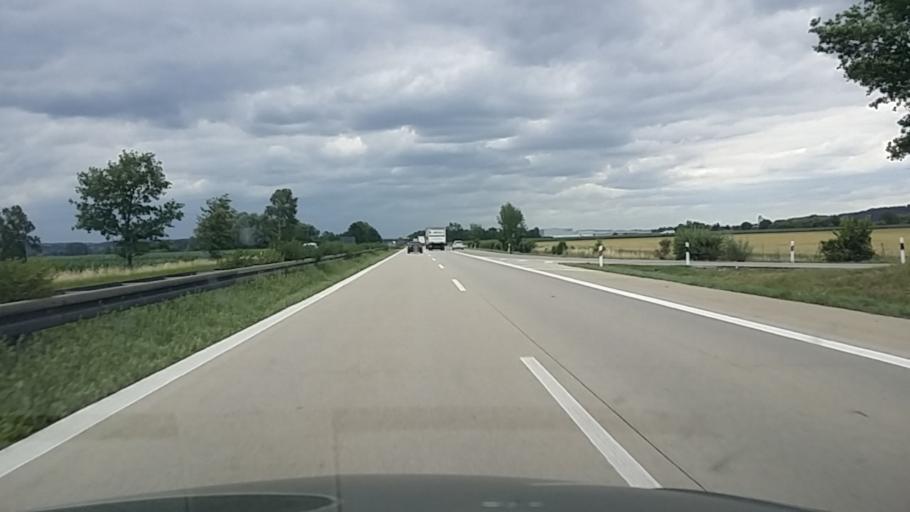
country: DE
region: Bavaria
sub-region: Lower Bavaria
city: Niederaichbach
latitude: 48.6190
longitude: 12.2935
